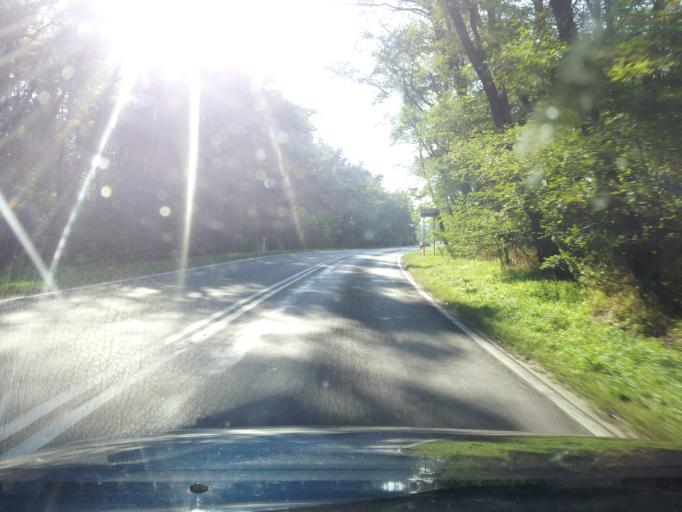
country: PL
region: Masovian Voivodeship
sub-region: Powiat nowodworski
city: Nowy Dwor Mazowiecki
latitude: 52.3943
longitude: 20.6723
